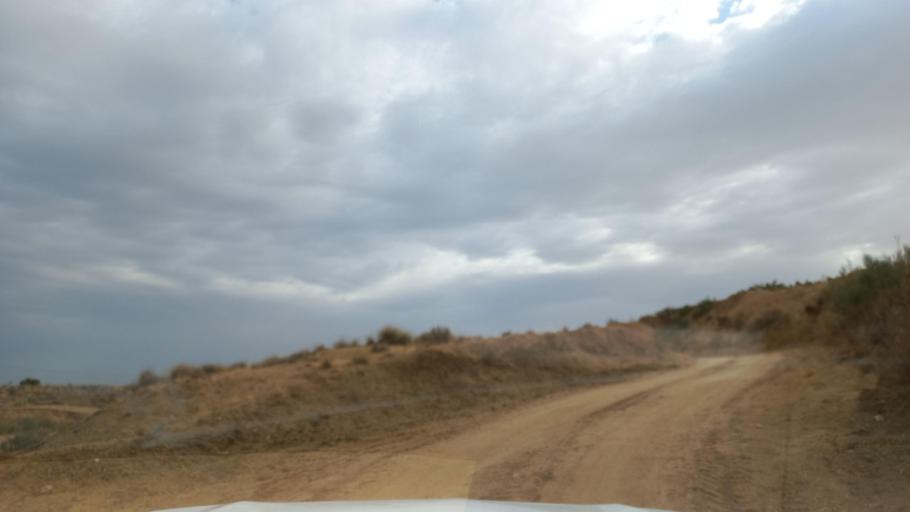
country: TN
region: Al Qasrayn
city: Kasserine
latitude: 35.1873
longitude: 9.0580
